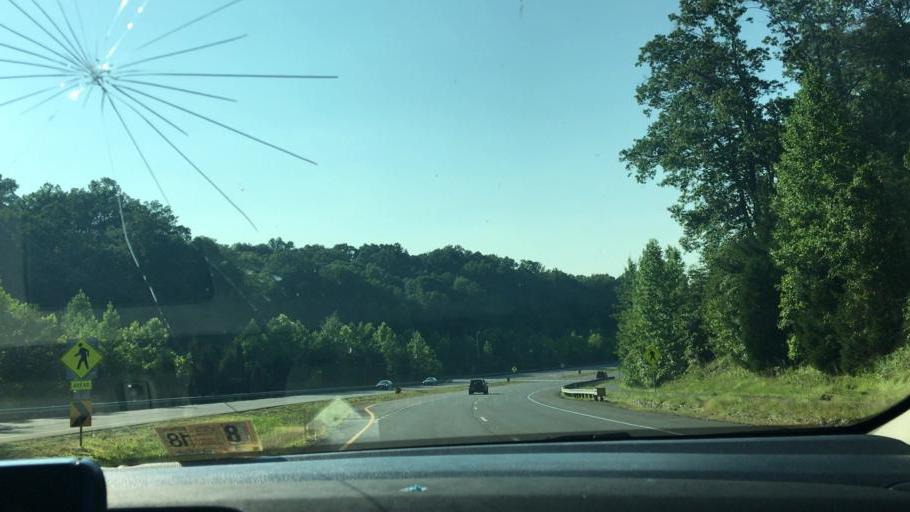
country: US
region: Virginia
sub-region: Prince William County
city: Buckhall
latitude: 38.6996
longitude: -77.4060
